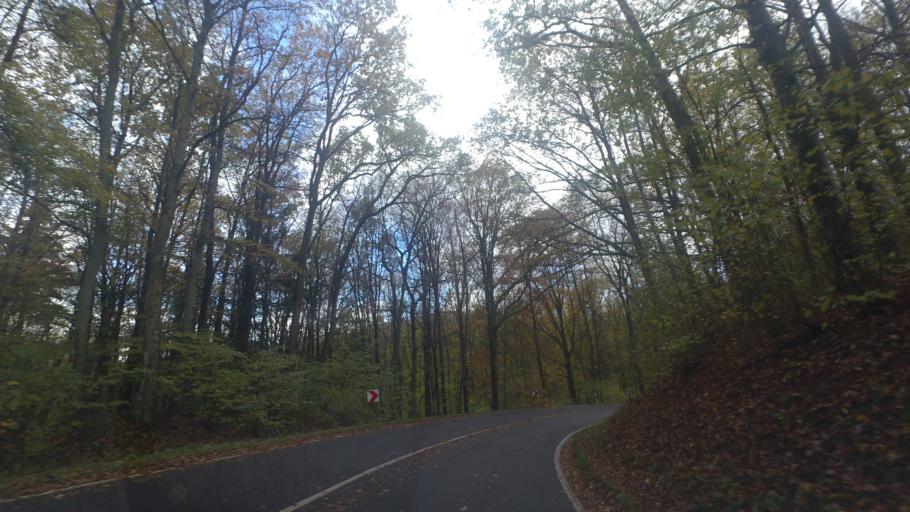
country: DE
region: Thuringia
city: Dingsleben
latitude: 50.4095
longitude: 10.6169
